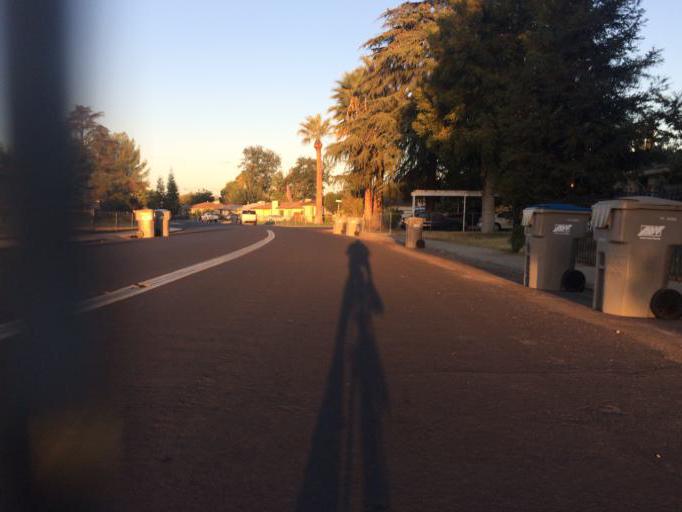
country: US
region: California
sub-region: Fresno County
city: Fresno
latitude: 36.7691
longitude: -119.7569
